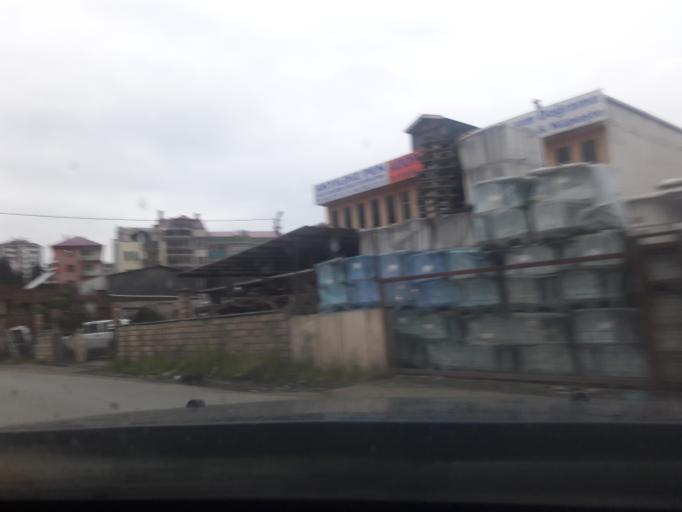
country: TR
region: Trabzon
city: Akcaabat
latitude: 41.0103
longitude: 39.5915
